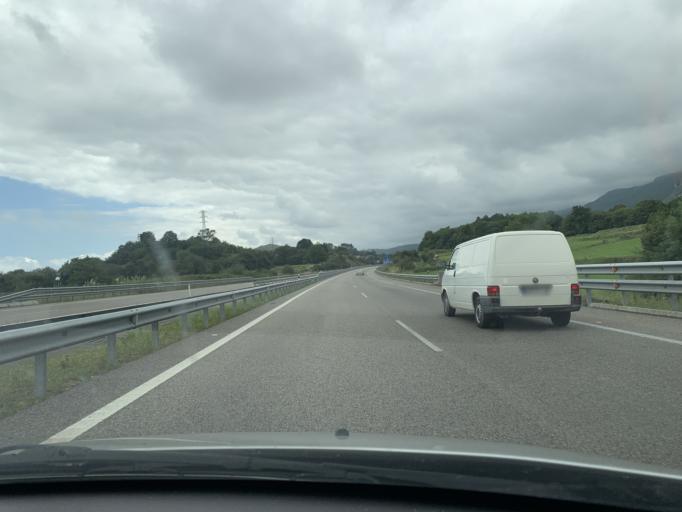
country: ES
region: Asturias
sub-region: Province of Asturias
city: Llanes
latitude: 43.4107
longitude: -4.7753
